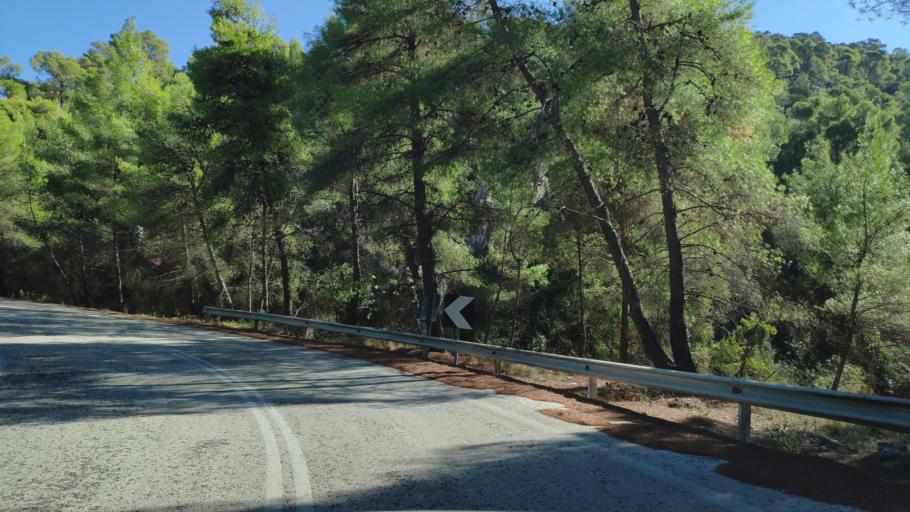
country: GR
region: Peloponnese
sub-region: Nomos Korinthias
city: Sofikon
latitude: 37.8269
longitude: 23.0656
